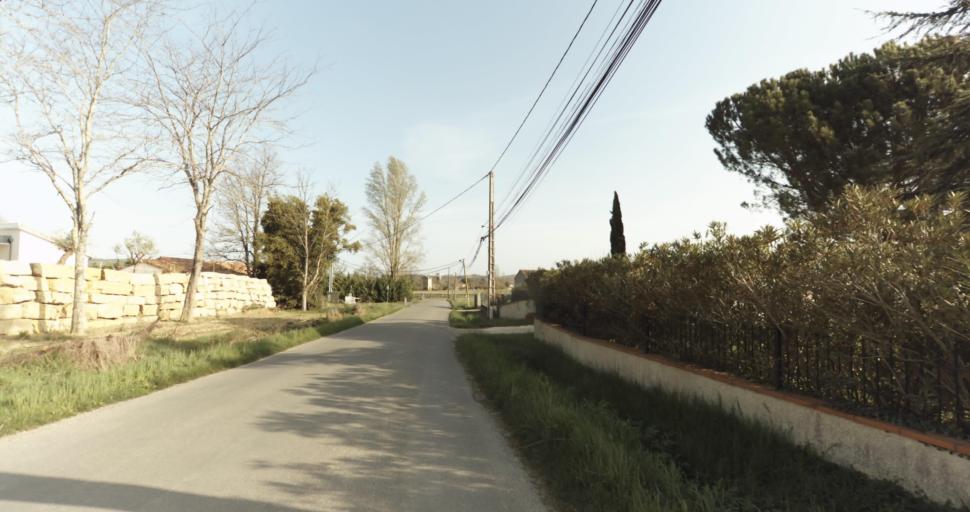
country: FR
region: Midi-Pyrenees
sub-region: Departement du Tarn
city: Saint-Sulpice-la-Pointe
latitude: 43.7658
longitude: 1.6770
